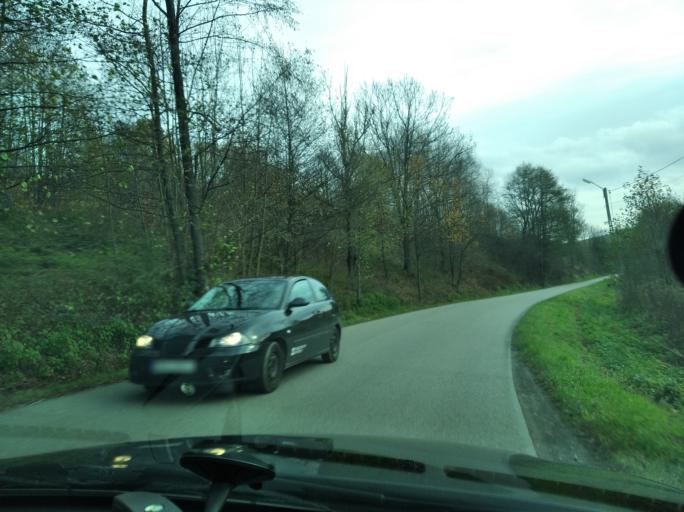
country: PL
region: Subcarpathian Voivodeship
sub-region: Powiat ropczycko-sedziszowski
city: Iwierzyce
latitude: 49.9507
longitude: 21.7283
